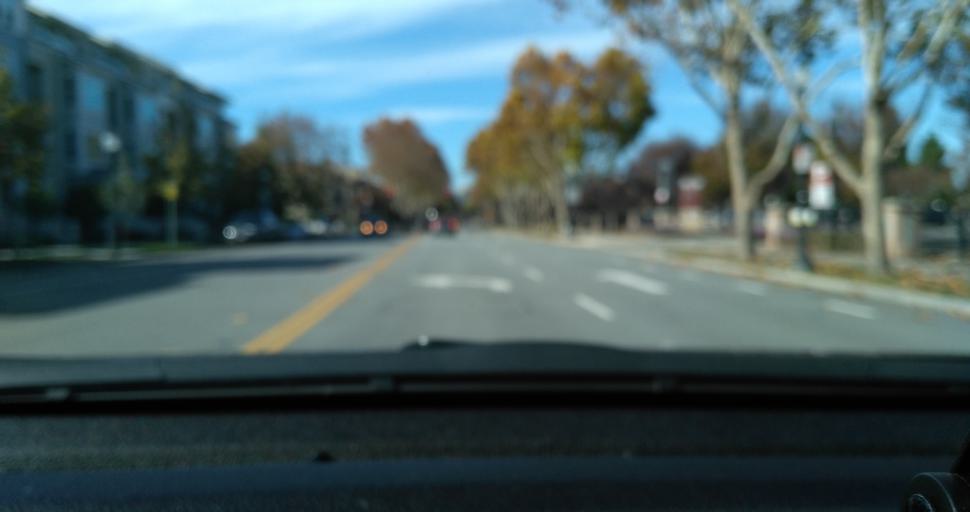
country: US
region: California
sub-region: Santa Clara County
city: Mountain View
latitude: 37.3930
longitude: -122.0738
